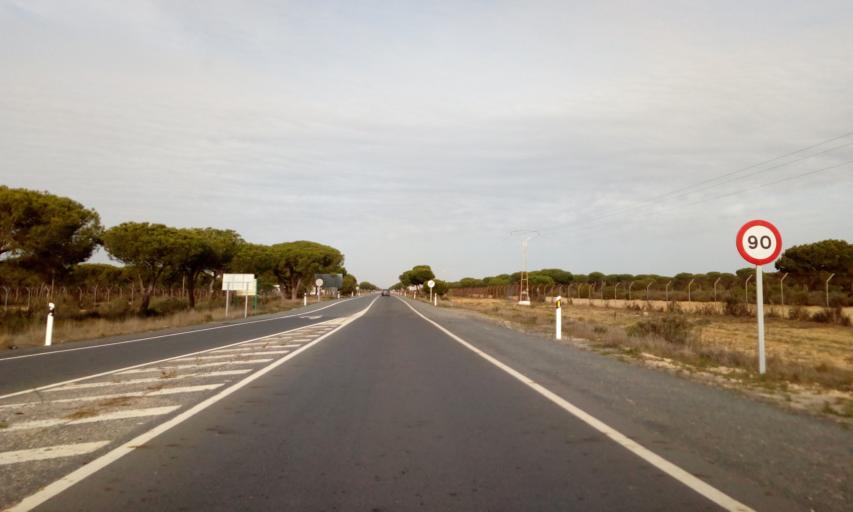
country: ES
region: Andalusia
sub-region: Provincia de Huelva
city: Mazagon
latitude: 37.0165
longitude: -6.5617
